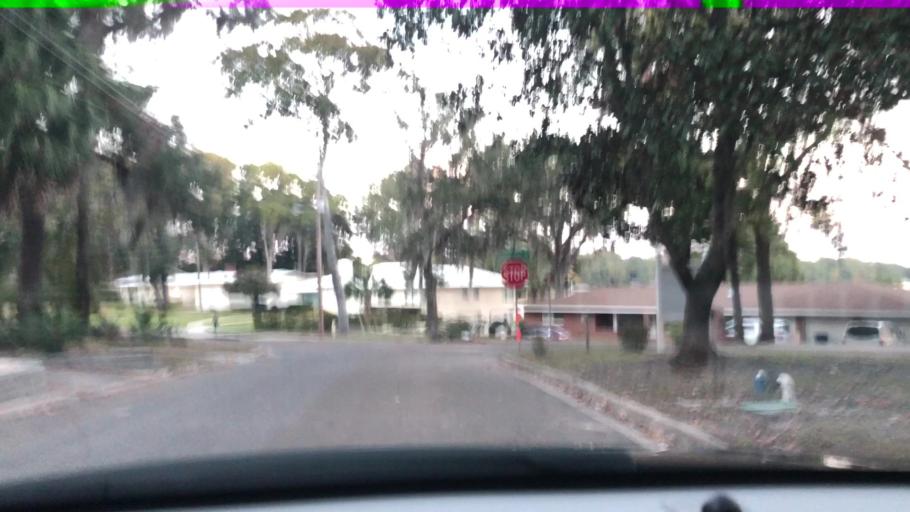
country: US
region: Florida
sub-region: Bay County
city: Panama City
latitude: 30.1370
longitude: -85.6383
